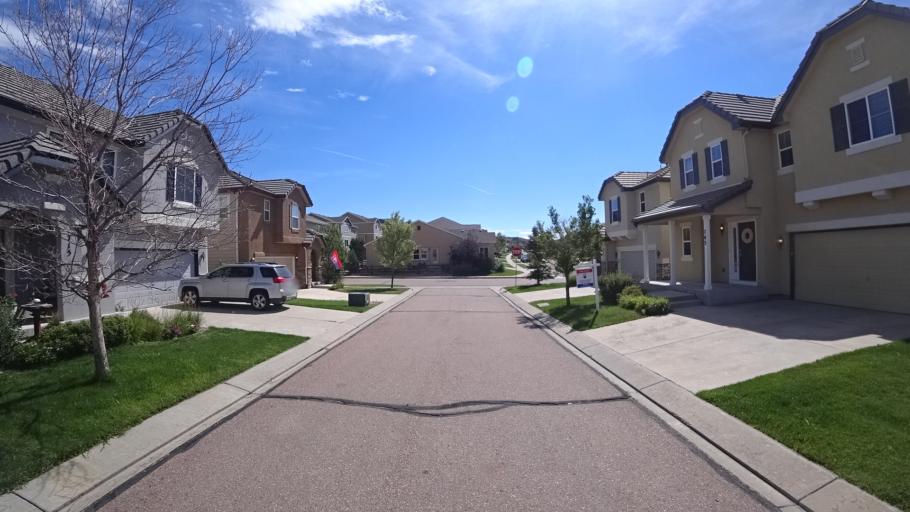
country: US
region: Colorado
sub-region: El Paso County
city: Gleneagle
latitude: 39.0246
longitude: -104.8135
